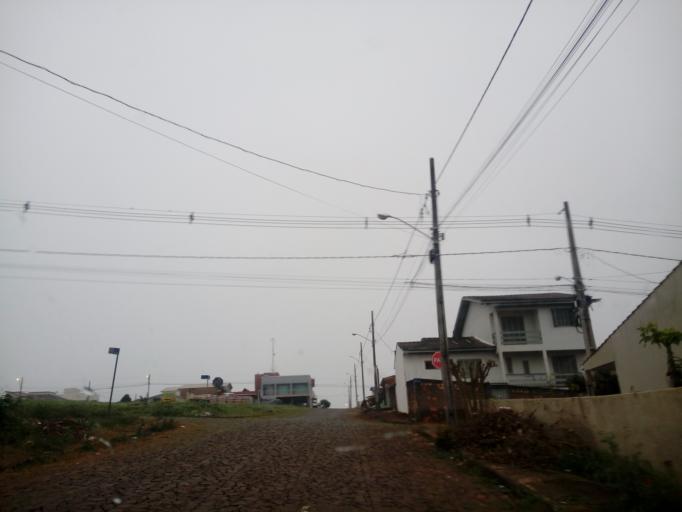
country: BR
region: Santa Catarina
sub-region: Chapeco
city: Chapeco
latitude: -27.1066
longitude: -52.6721
